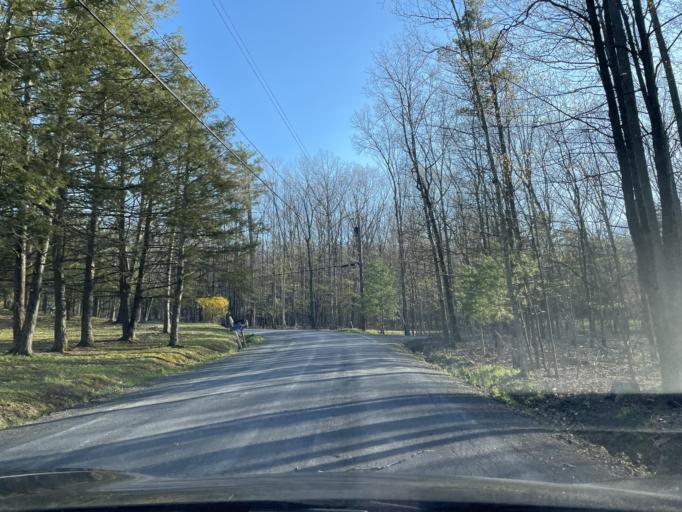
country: US
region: New York
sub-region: Ulster County
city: Woodstock
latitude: 42.0311
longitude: -74.1140
